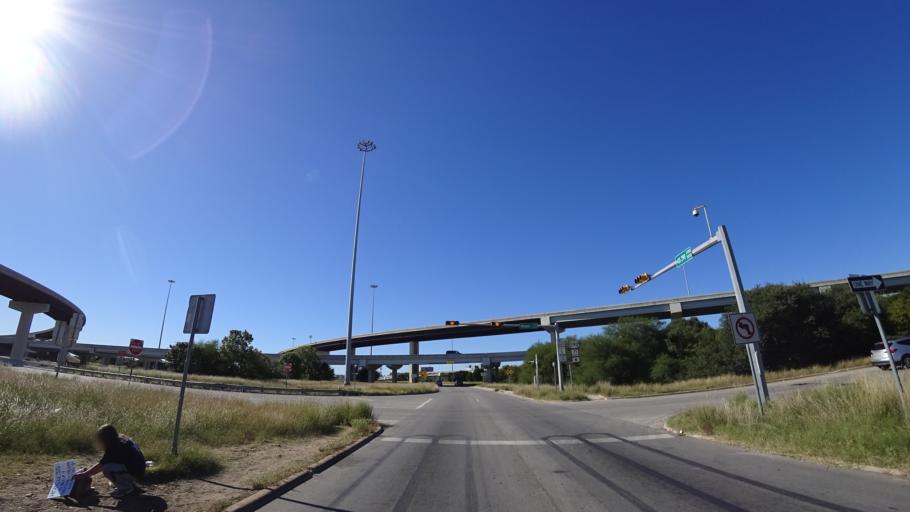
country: US
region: Texas
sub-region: Travis County
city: Rollingwood
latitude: 30.2356
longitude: -97.8229
